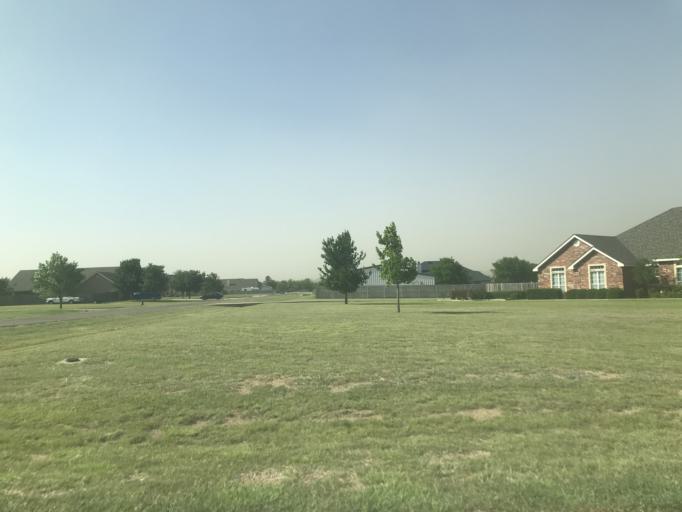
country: US
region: Texas
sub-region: Taylor County
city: Potosi
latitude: 32.3387
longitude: -99.7135
